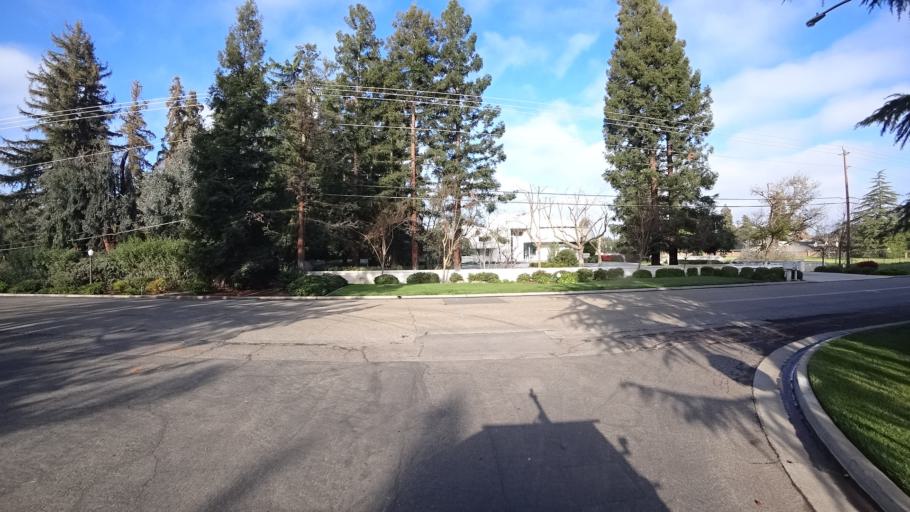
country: US
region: California
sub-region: Fresno County
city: Fresno
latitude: 36.8256
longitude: -119.8307
